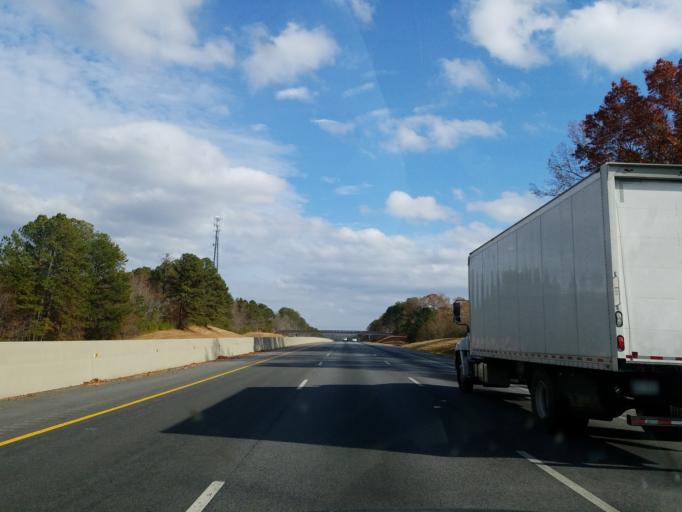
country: US
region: Alabama
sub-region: Cleburne County
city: Heflin
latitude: 33.6455
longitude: -85.4652
